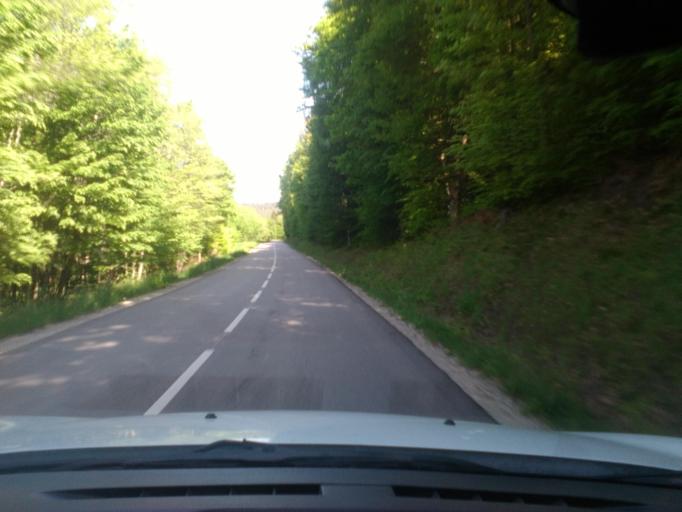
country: FR
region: Lorraine
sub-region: Departement des Vosges
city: Bruyeres
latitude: 48.2610
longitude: 6.7263
